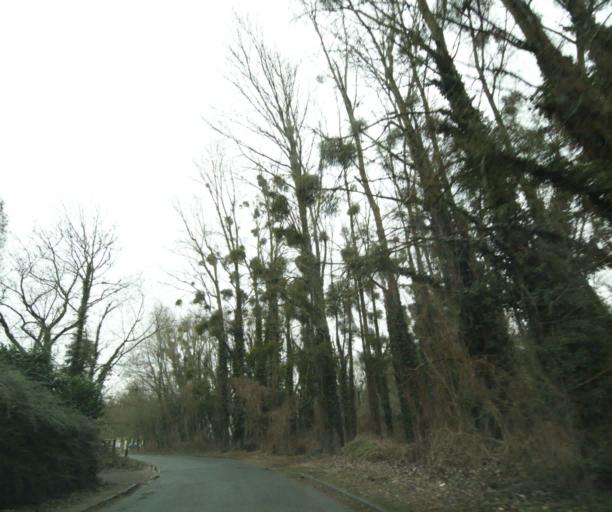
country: FR
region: Ile-de-France
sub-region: Departement de l'Essonne
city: Champlan
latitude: 48.7018
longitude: 2.2710
